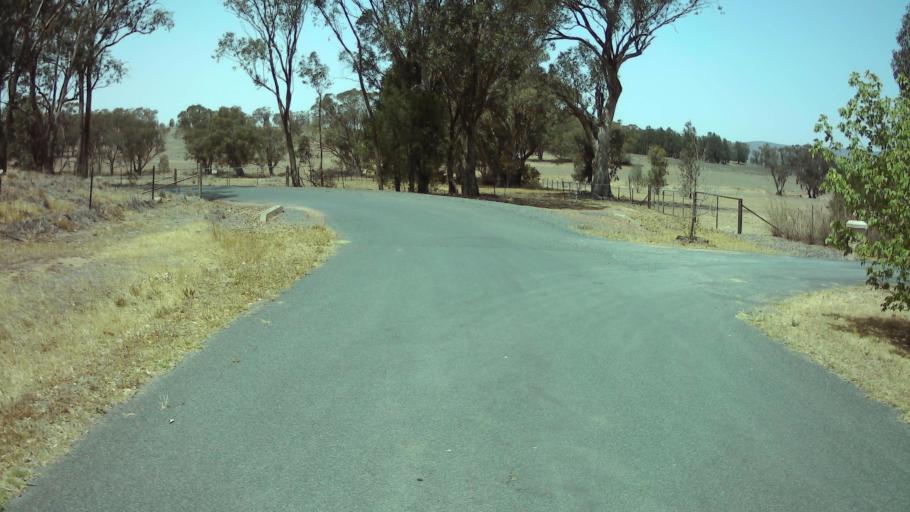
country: AU
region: New South Wales
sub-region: Weddin
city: Grenfell
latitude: -33.9109
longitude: 148.1503
